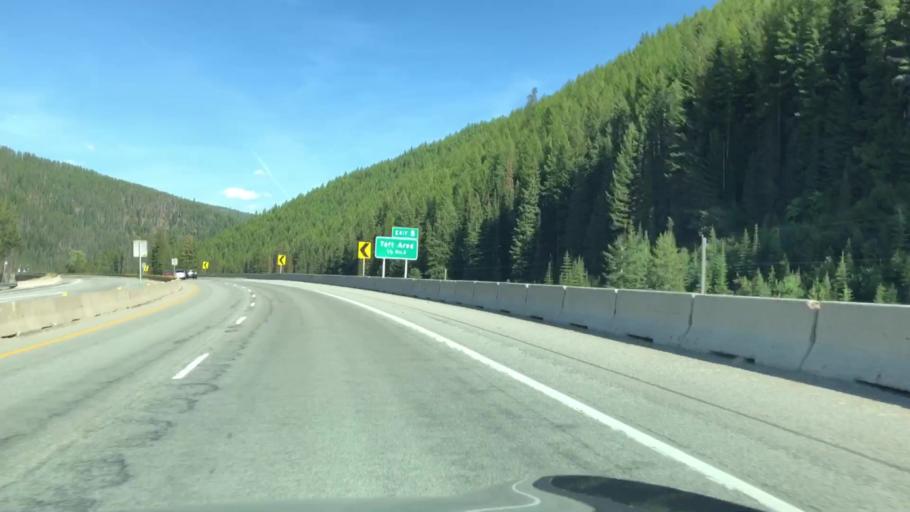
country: US
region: Idaho
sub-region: Shoshone County
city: Wallace
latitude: 47.4182
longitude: -115.6205
